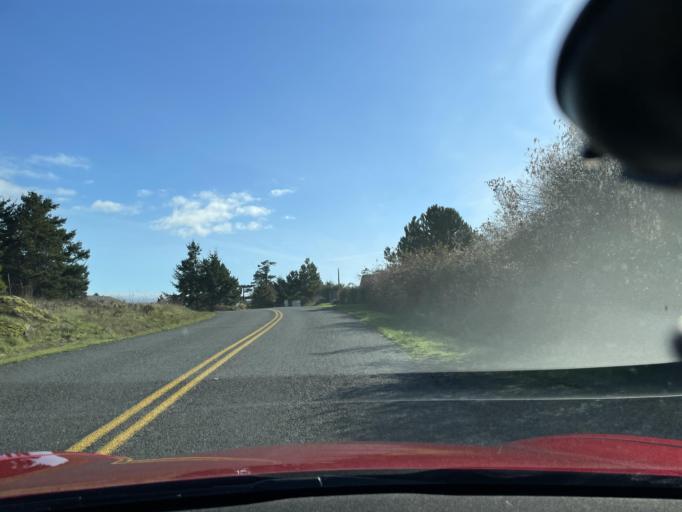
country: US
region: Washington
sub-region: San Juan County
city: Friday Harbor
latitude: 48.4574
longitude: -122.9660
